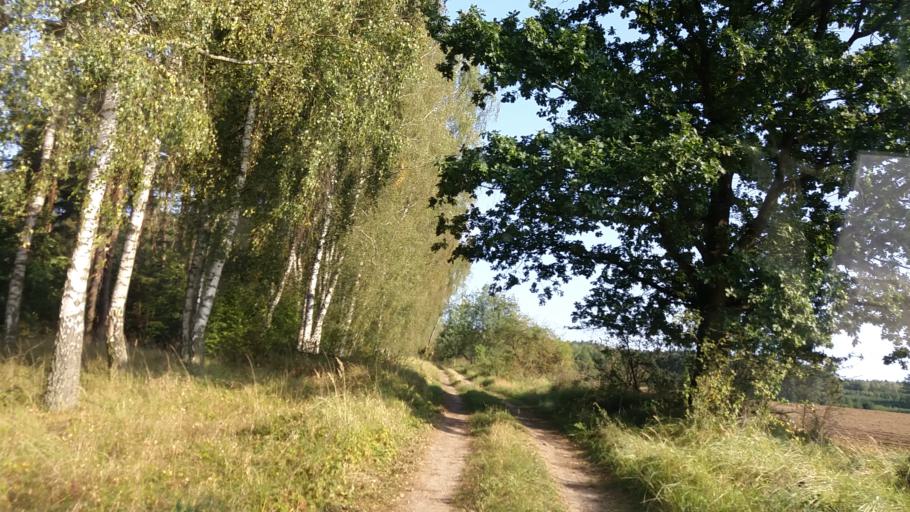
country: PL
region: West Pomeranian Voivodeship
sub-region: Powiat choszczenski
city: Recz
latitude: 53.1891
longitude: 15.5413
